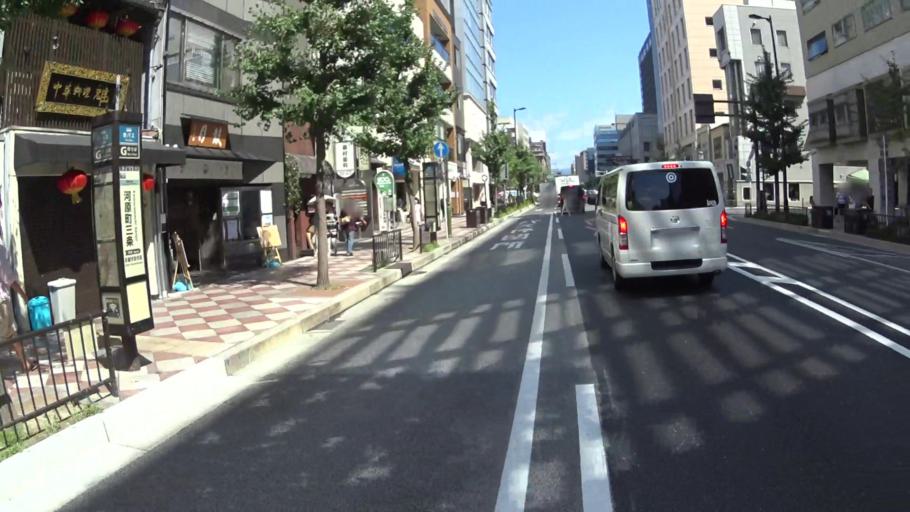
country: JP
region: Kyoto
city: Kyoto
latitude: 35.0092
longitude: 135.7693
